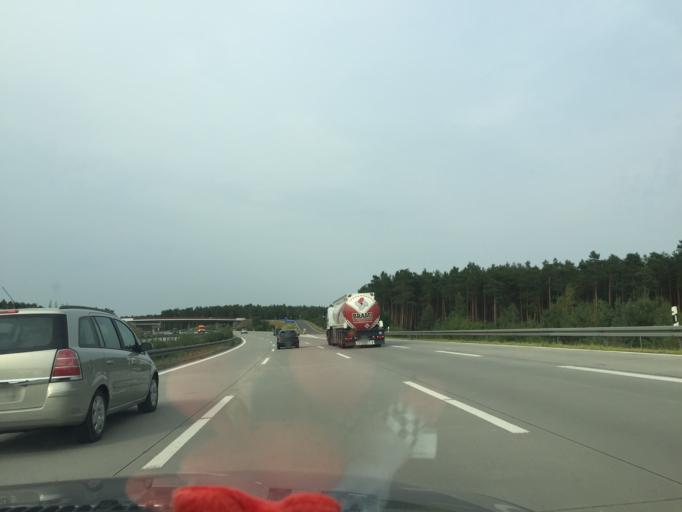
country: DE
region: Brandenburg
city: Erkner
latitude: 52.3858
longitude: 13.7851
